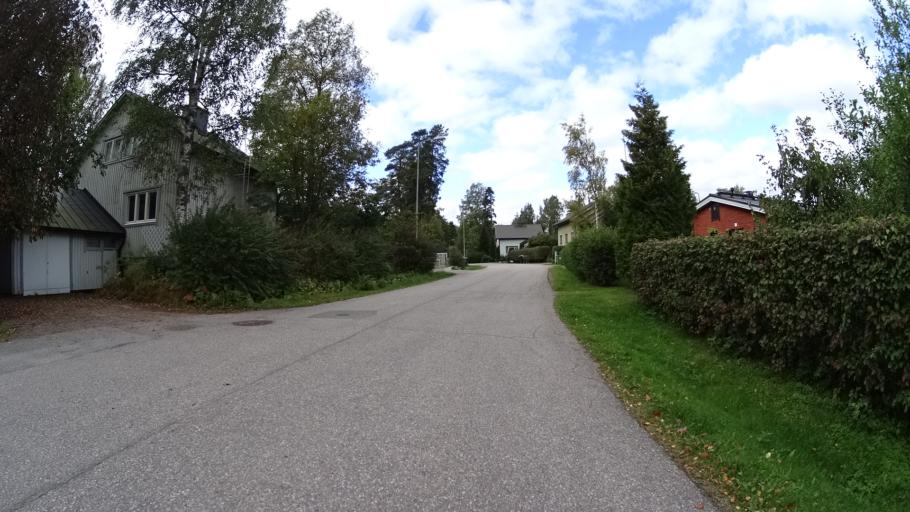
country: FI
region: Uusimaa
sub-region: Helsinki
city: Helsinki
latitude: 60.2496
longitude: 24.9027
